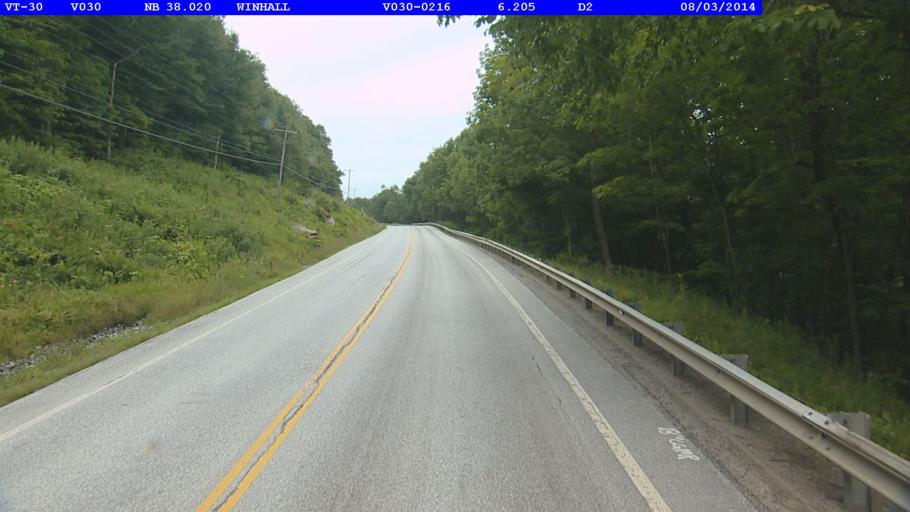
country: US
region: Vermont
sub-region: Bennington County
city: Manchester Center
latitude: 43.1920
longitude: -72.9457
